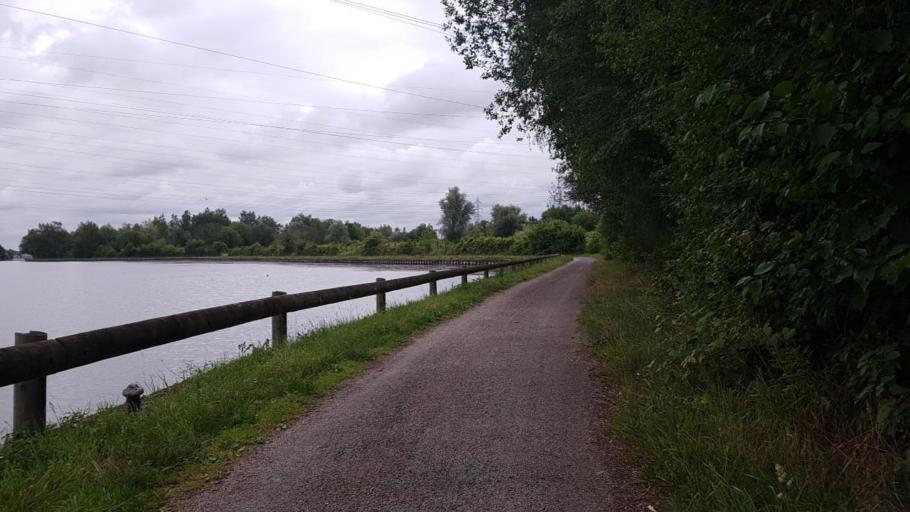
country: FR
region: Picardie
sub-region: Departement de l'Aisne
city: Beautor
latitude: 49.6523
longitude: 3.3255
